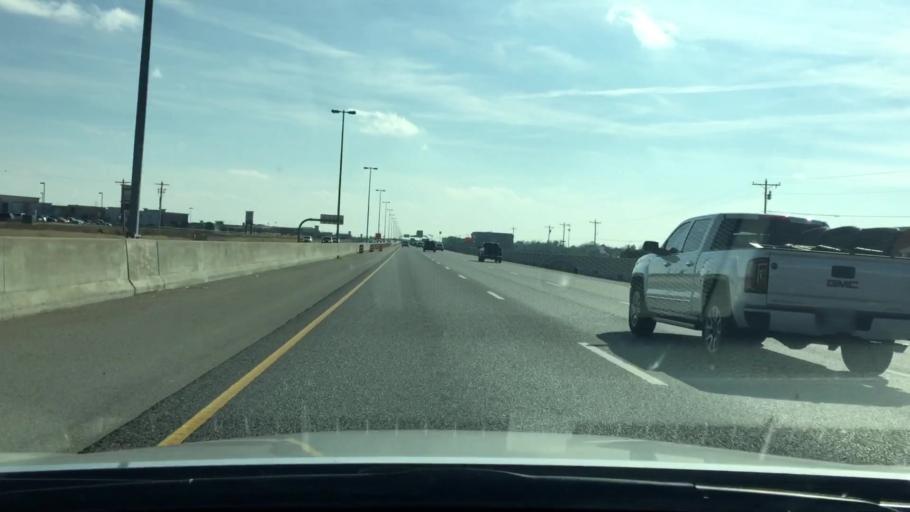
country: US
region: Oklahoma
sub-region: Cleveland County
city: Norman
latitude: 35.2473
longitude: -97.4856
